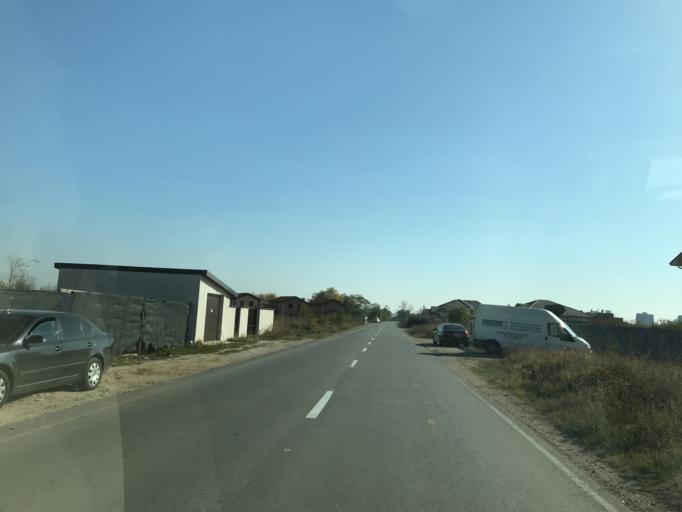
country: RO
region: Olt
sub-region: Municipiul Slatina
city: Slatina
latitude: 44.4405
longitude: 24.3597
